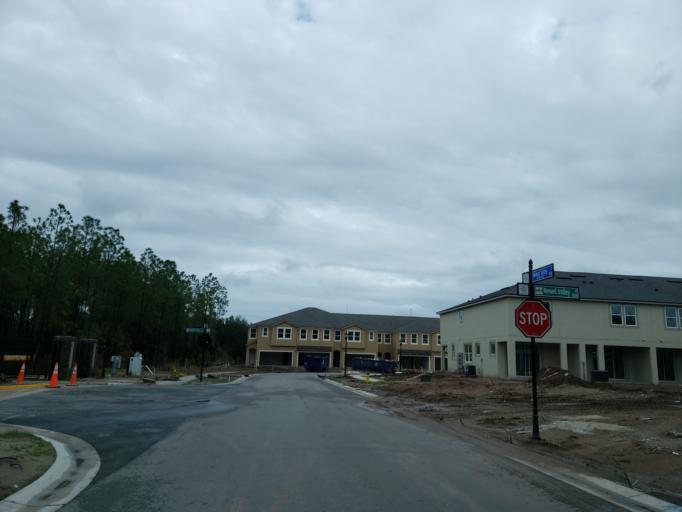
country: US
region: Florida
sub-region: Hillsborough County
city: Riverview
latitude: 27.8528
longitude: -82.3076
